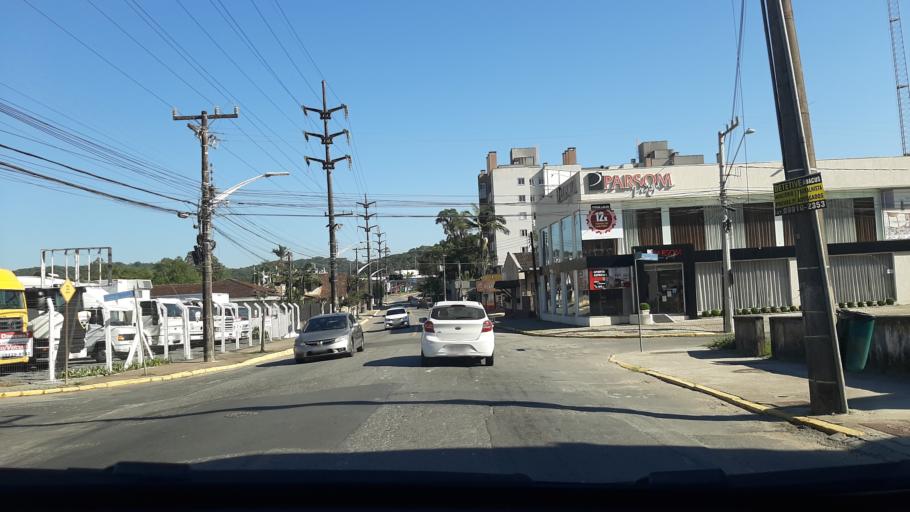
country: BR
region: Santa Catarina
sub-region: Joinville
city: Joinville
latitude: -26.3187
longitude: -48.8681
